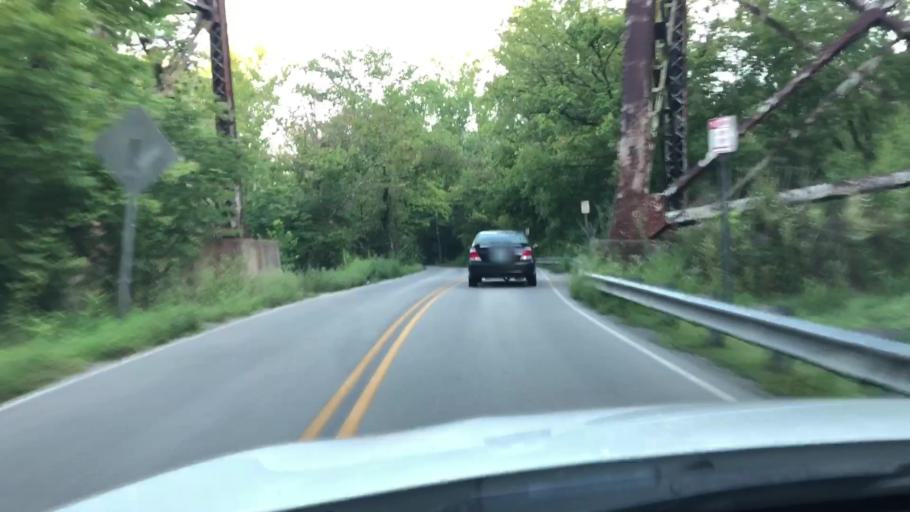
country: US
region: Kentucky
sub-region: Jefferson County
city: Middletown
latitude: 38.1918
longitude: -85.4876
